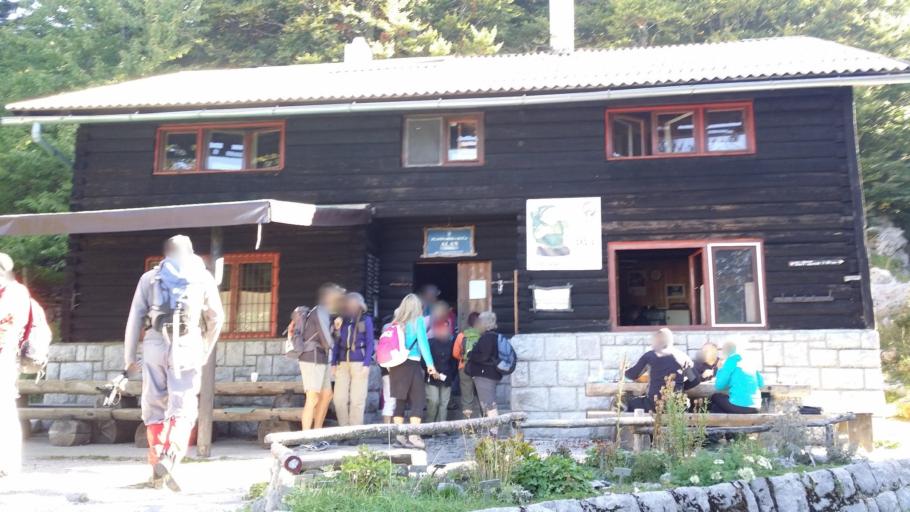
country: HR
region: Licko-Senjska
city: Novalja
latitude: 44.7214
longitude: 14.9691
